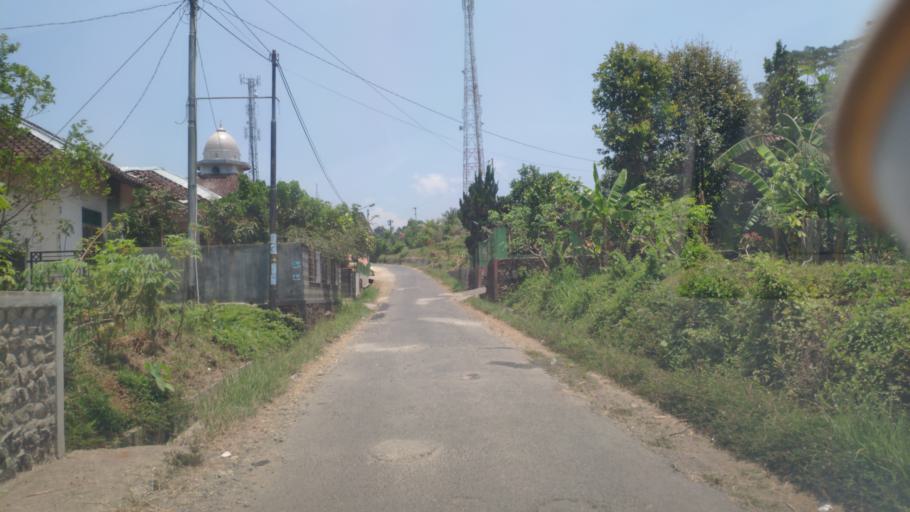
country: ID
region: Central Java
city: Wonosobo
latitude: -7.4008
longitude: 109.6627
